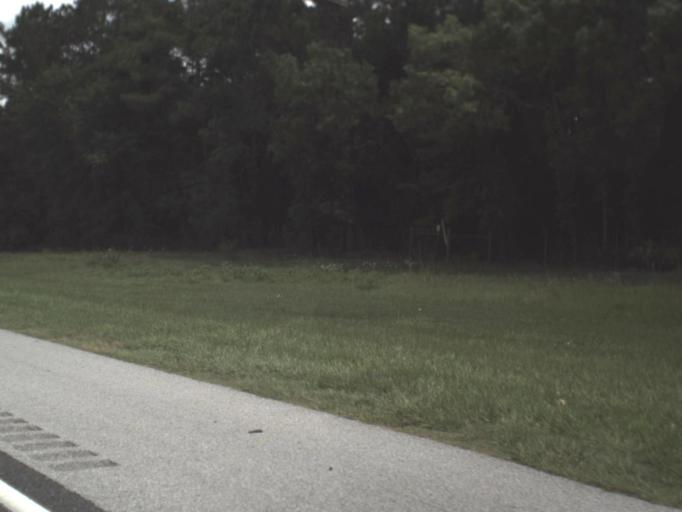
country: US
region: Florida
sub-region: Suwannee County
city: Wellborn
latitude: 30.3348
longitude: -82.8234
